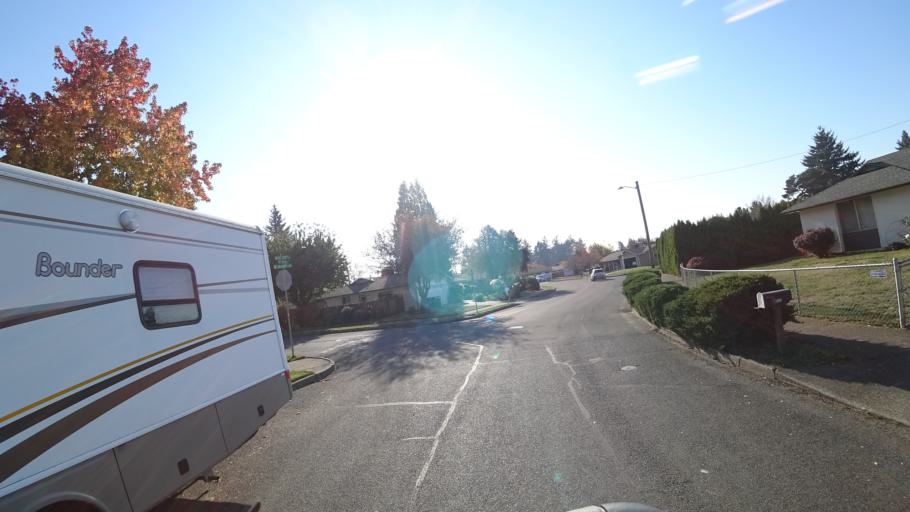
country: US
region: Oregon
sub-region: Multnomah County
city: Gresham
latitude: 45.5141
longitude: -122.4317
